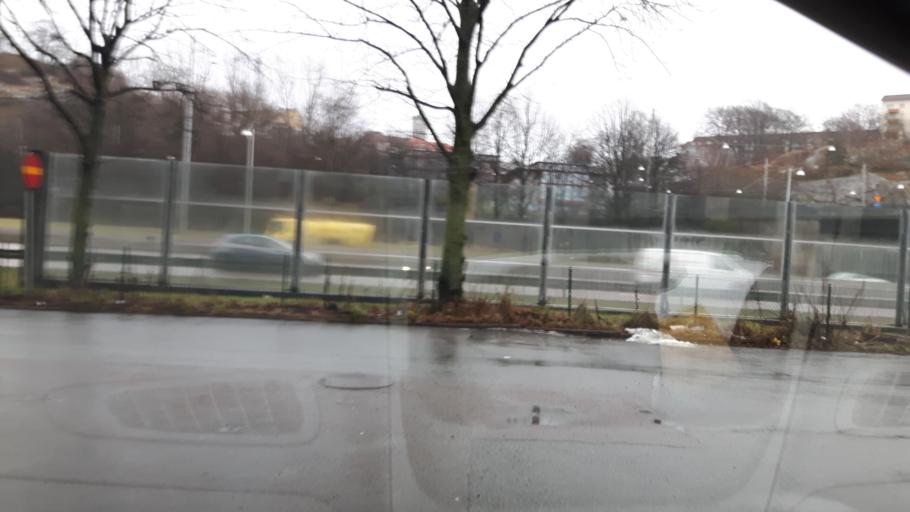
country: SE
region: Vaestra Goetaland
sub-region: Goteborg
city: Goeteborg
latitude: 57.7098
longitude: 11.9961
